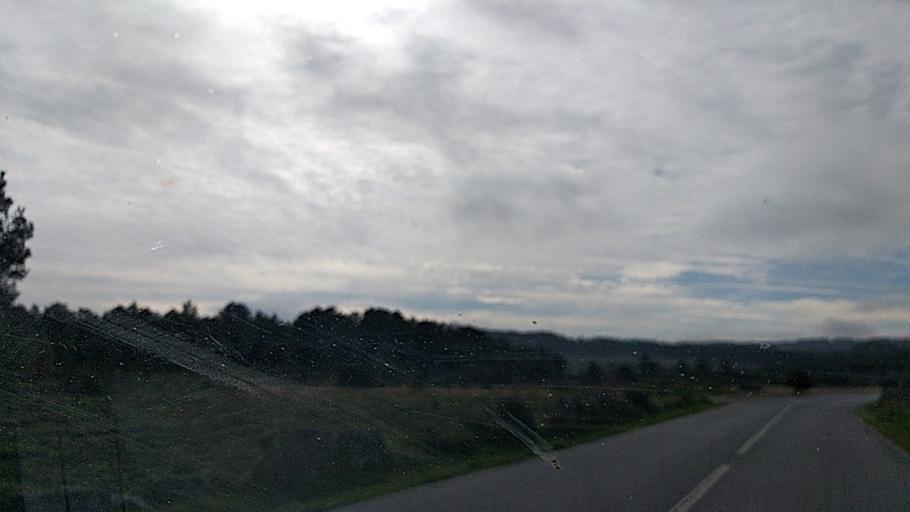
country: PT
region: Guarda
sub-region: Fornos de Algodres
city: Fornos de Algodres
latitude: 40.6724
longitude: -7.5289
